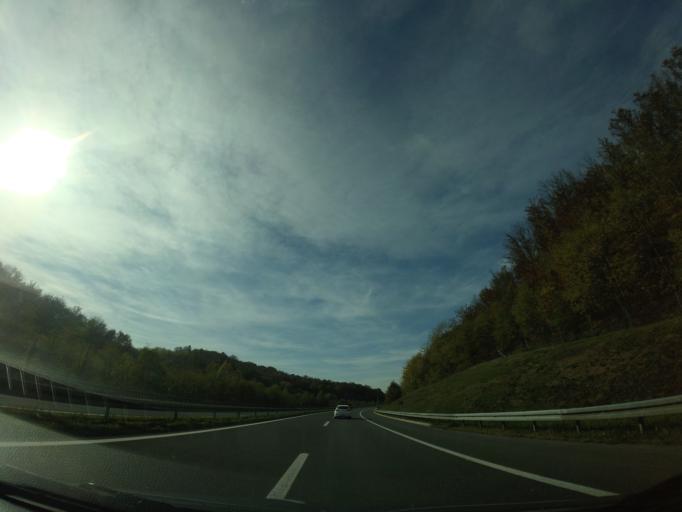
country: HR
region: Varazdinska
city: Remetinec
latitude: 46.1277
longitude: 16.3342
